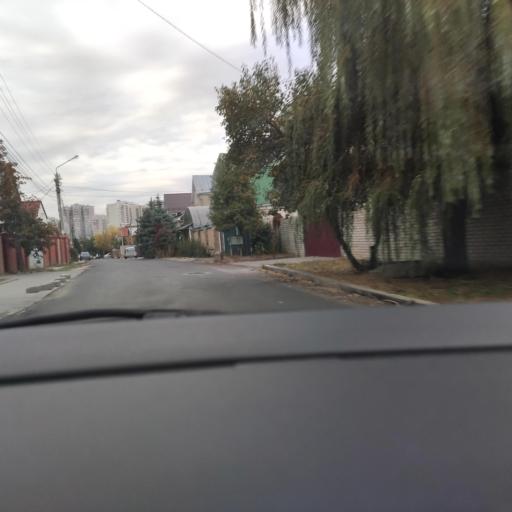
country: RU
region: Voronezj
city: Voronezh
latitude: 51.7050
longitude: 39.2042
